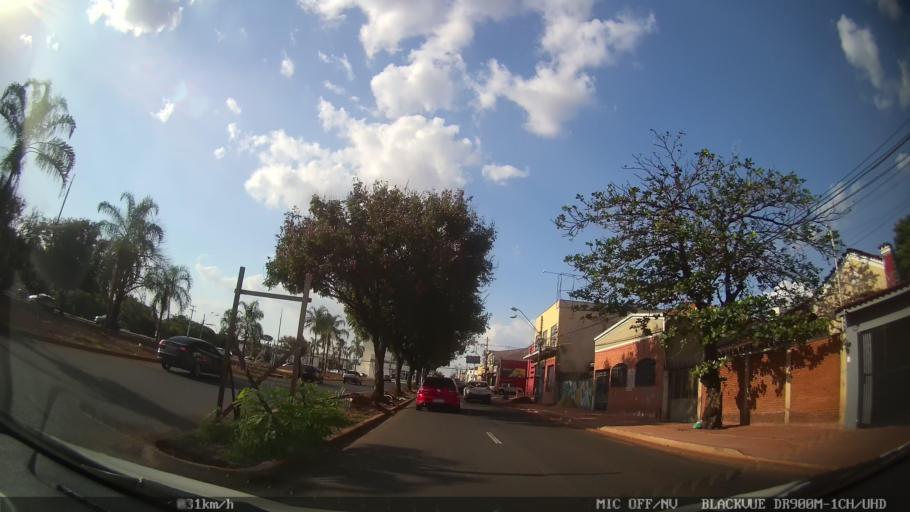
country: BR
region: Sao Paulo
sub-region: Ribeirao Preto
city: Ribeirao Preto
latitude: -21.1637
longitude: -47.8117
